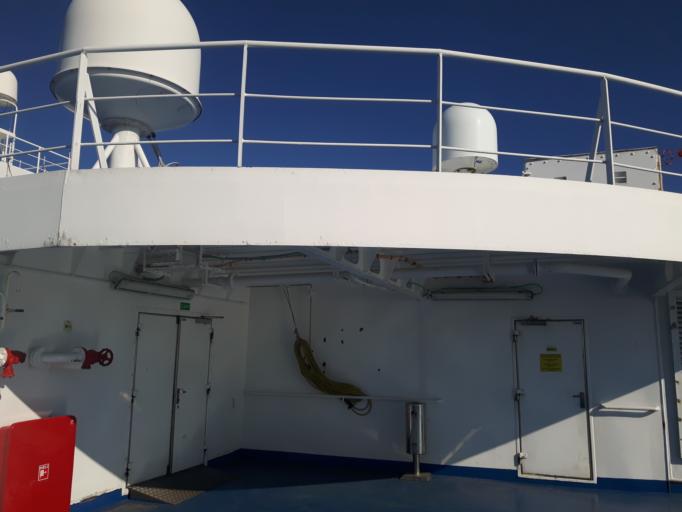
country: SE
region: Gotland
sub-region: Gotland
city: Hemse
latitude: 56.5980
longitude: 17.9607
